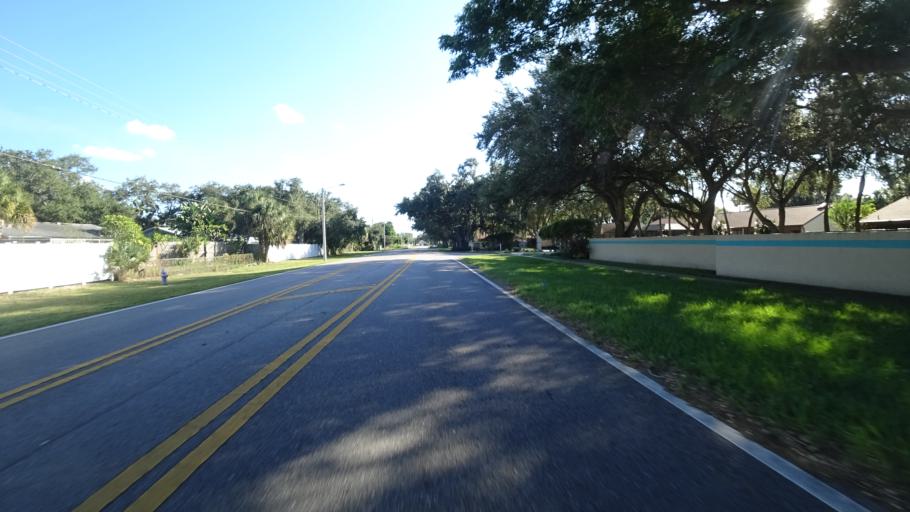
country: US
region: Florida
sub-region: Manatee County
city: South Bradenton
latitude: 27.4751
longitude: -82.6041
